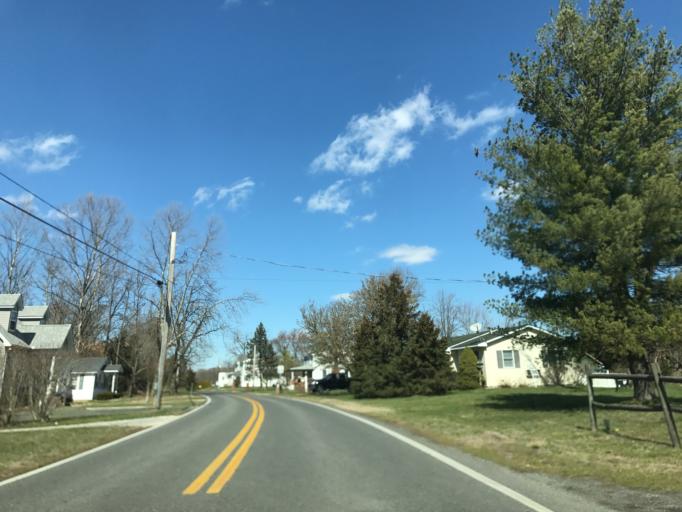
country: US
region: Maryland
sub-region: Queen Anne's County
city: Kingstown
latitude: 39.1492
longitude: -75.9786
